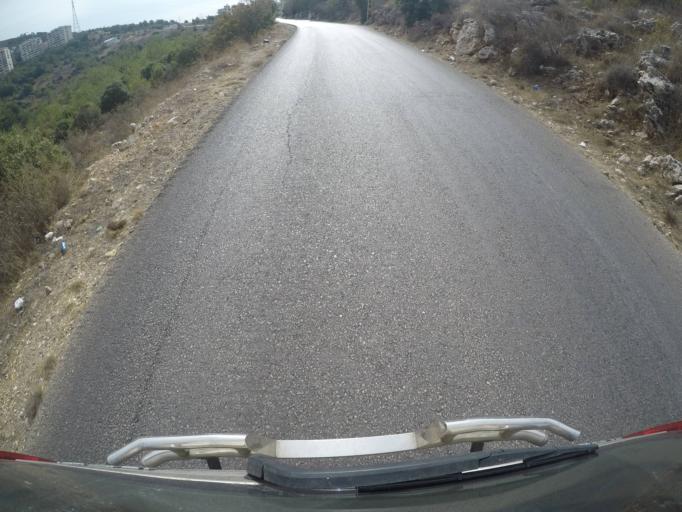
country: LB
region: Mont-Liban
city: Beit ed Dine
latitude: 33.7364
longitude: 35.4838
